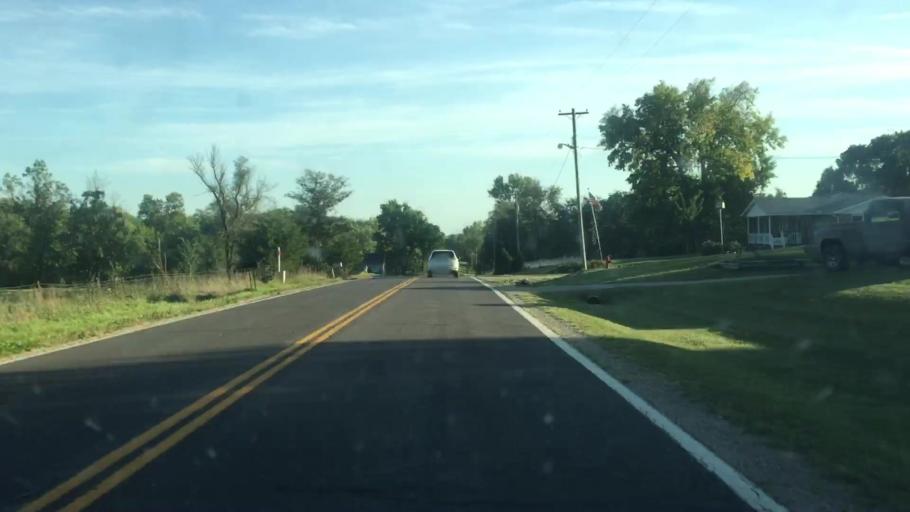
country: US
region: Kansas
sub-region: Brown County
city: Horton
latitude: 39.5550
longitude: -95.5247
